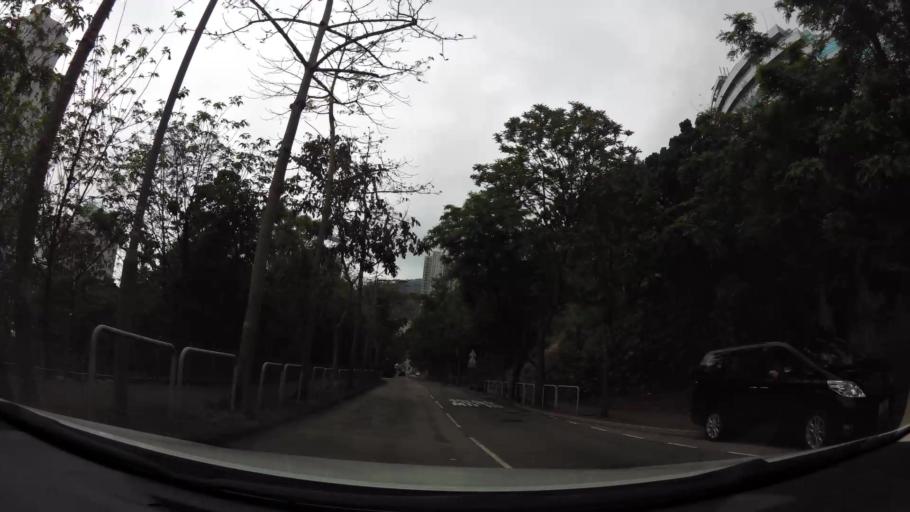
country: HK
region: Central and Western
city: Central
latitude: 22.2667
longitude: 114.1278
